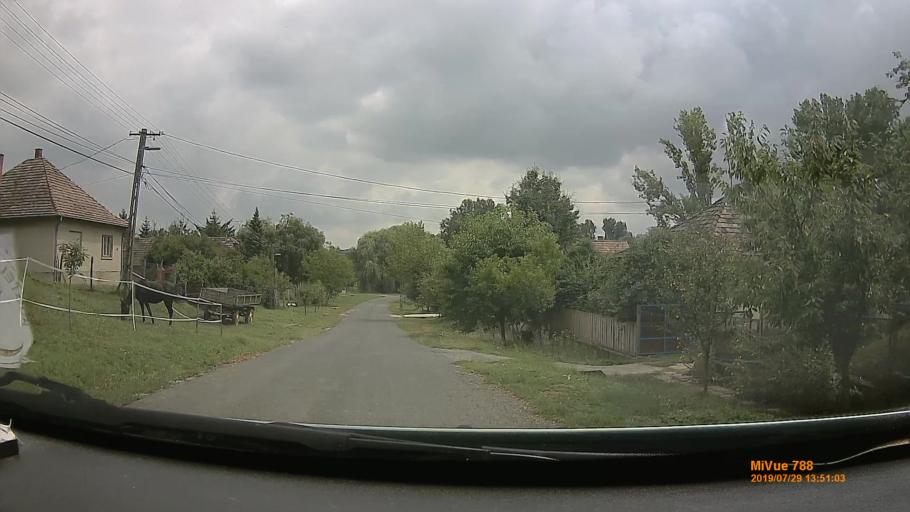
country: HU
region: Somogy
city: Tab
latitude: 46.7756
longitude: 17.9584
